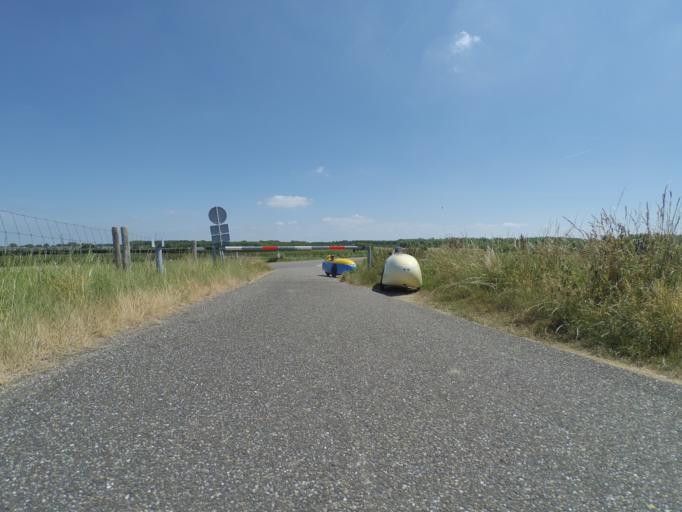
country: NL
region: Zeeland
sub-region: Gemeente Reimerswaal
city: Yerseke
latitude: 51.5432
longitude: 4.0625
